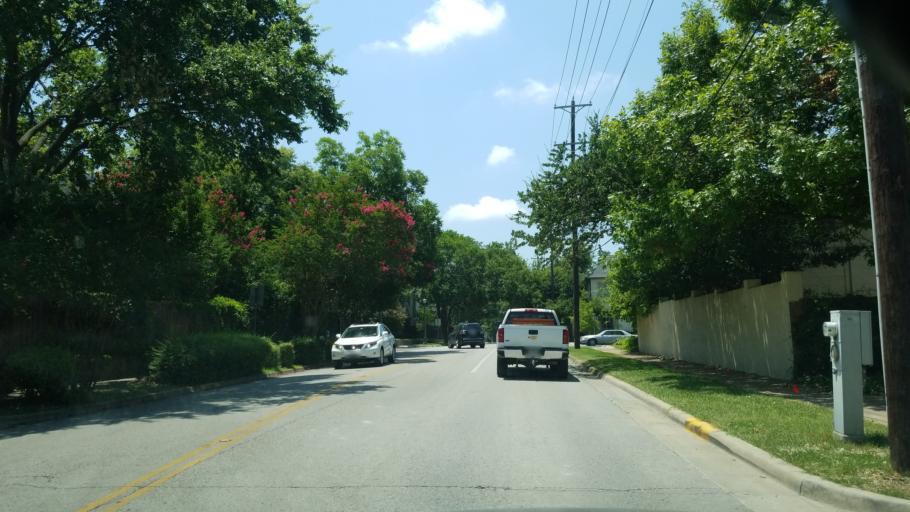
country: US
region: Texas
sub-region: Dallas County
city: Highland Park
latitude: 32.8361
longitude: -96.7872
